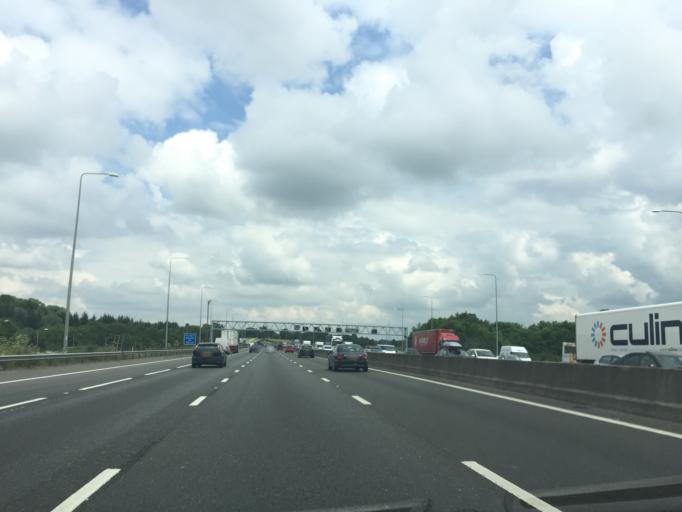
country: GB
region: England
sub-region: Hertfordshire
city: Kings Langley
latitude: 51.6788
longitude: -0.4557
